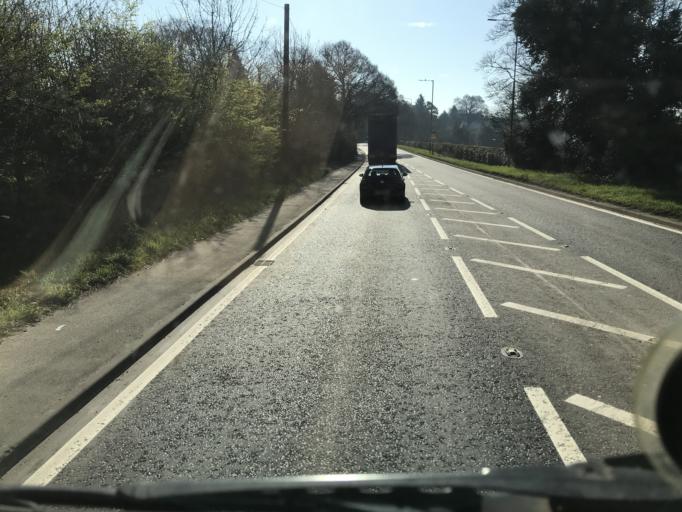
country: GB
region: England
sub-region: Cheshire West and Chester
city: Guilden Sutton
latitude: 53.1806
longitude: -2.8383
